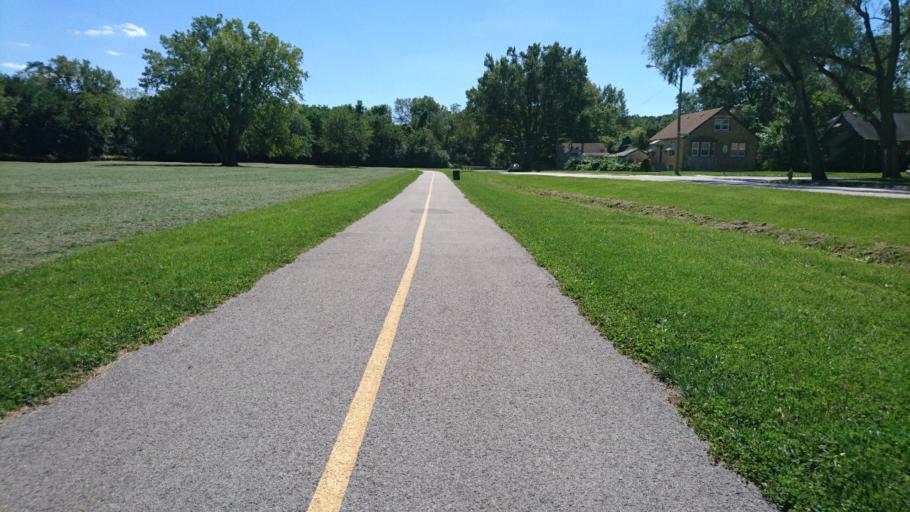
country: US
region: Illinois
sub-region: Cook County
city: Chicago Heights
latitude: 41.5165
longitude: -87.6331
